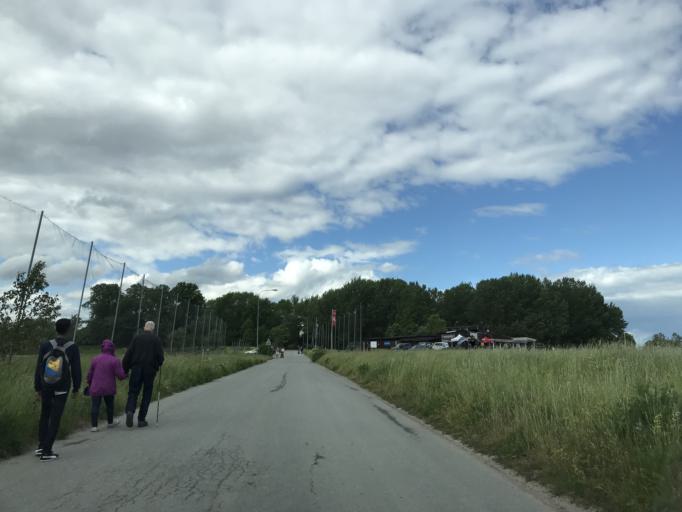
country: SE
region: Stockholm
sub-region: Solna Kommun
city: Rasunda
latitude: 59.3855
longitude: 17.9979
